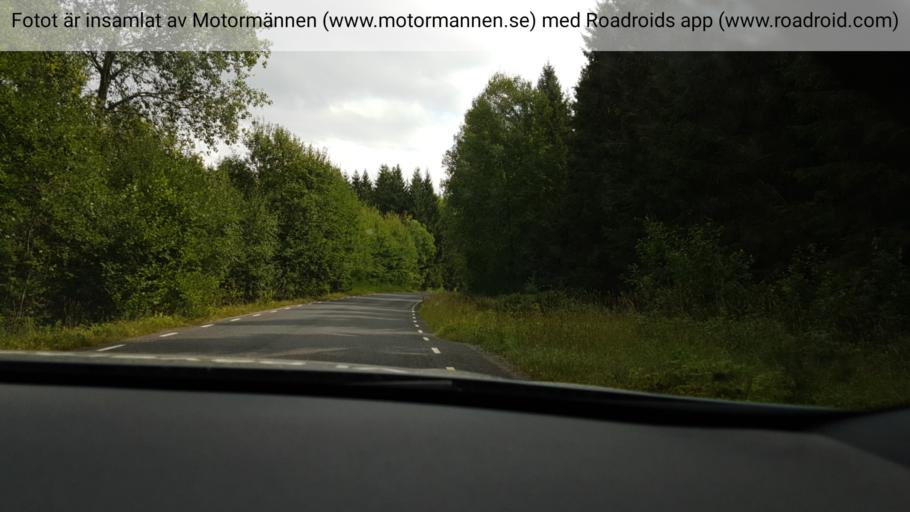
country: SE
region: Vaestra Goetaland
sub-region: Falkopings Kommun
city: Floby
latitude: 58.1255
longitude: 13.3972
